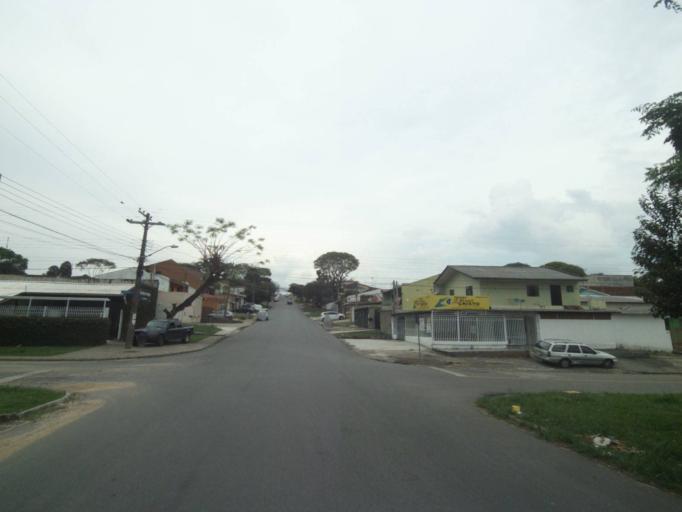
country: BR
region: Parana
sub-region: Pinhais
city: Pinhais
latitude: -25.4016
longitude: -49.2103
